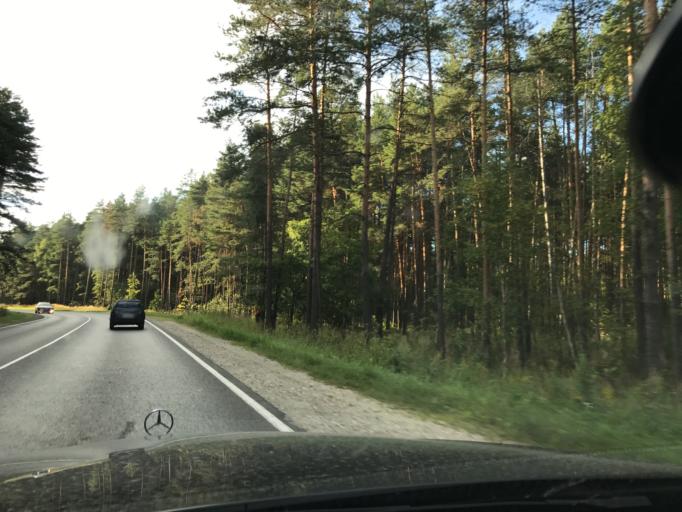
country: RU
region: Vladimir
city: Raduzhnyy
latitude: 56.0297
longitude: 40.3774
